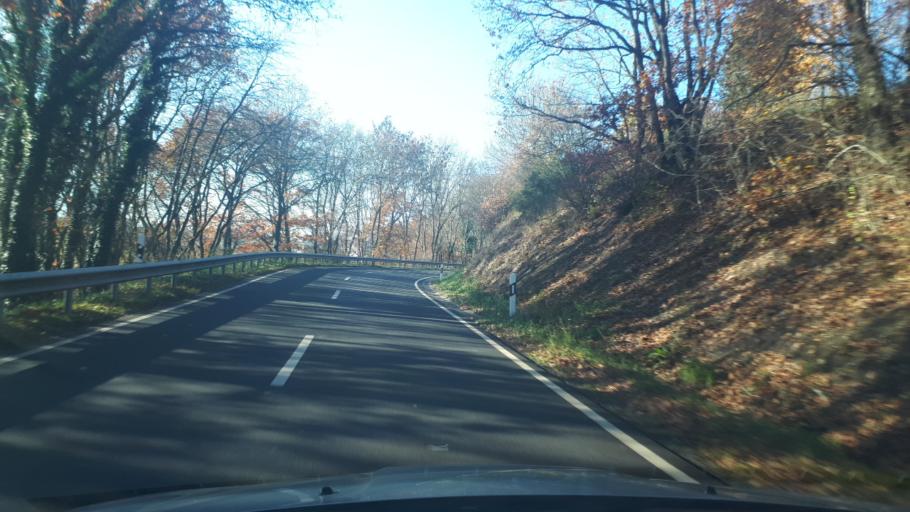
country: DE
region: Rheinland-Pfalz
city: Weiler
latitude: 50.1550
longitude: 7.0943
